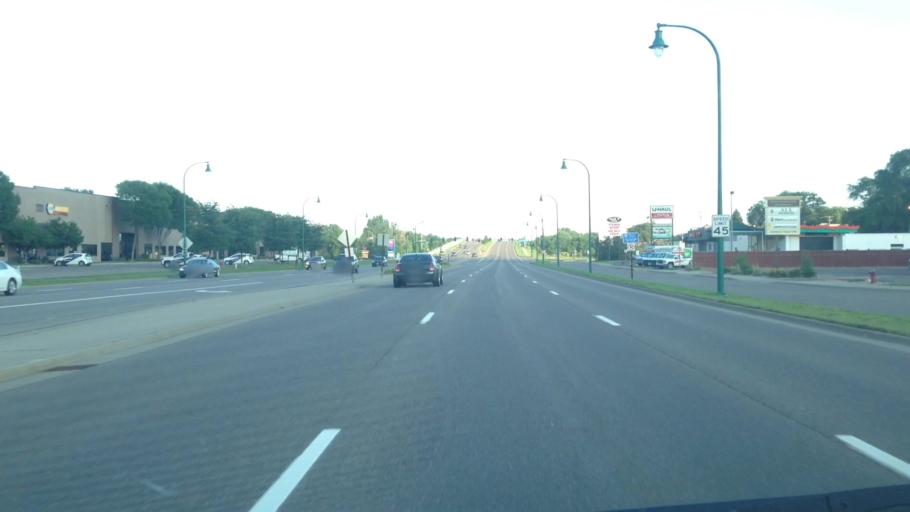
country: US
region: Minnesota
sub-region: Hennepin County
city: Crystal
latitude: 45.0535
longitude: -93.3573
